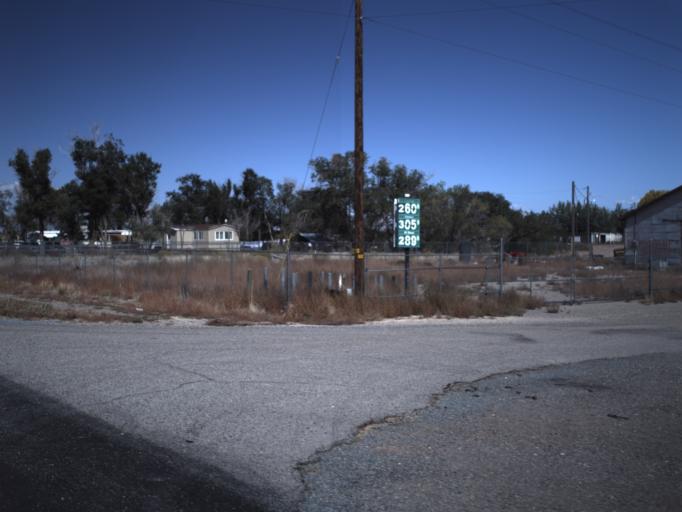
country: US
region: Utah
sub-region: Washington County
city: Enterprise
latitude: 37.6921
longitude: -113.6564
